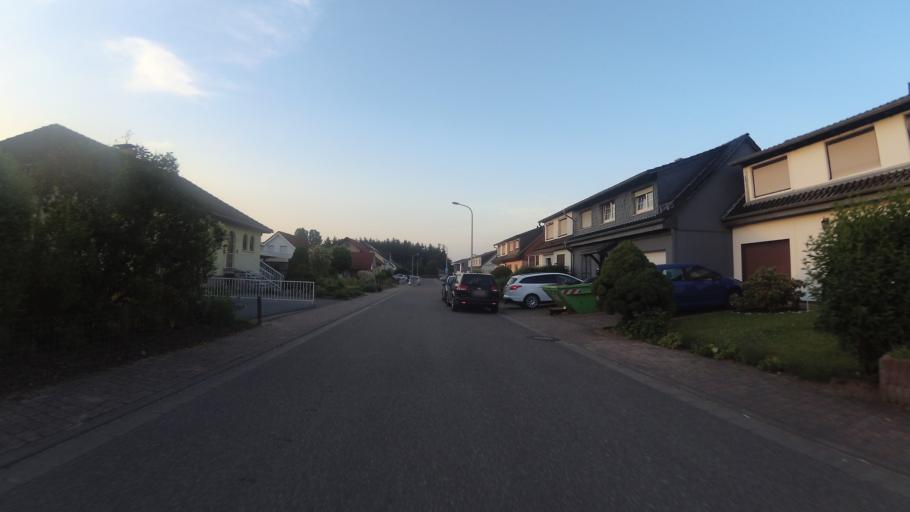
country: DE
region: Rheinland-Pfalz
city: Bruchmuhlbach-Miesau
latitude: 49.4027
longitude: 7.4274
